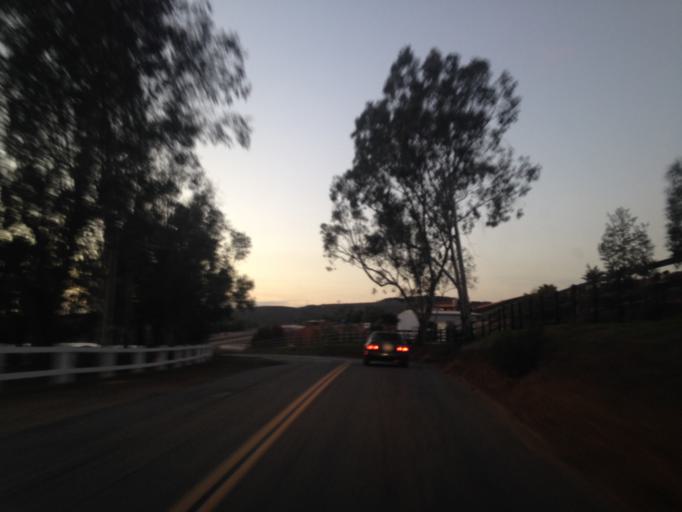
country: US
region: California
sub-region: San Diego County
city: Bonsall
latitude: 33.2666
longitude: -117.2285
